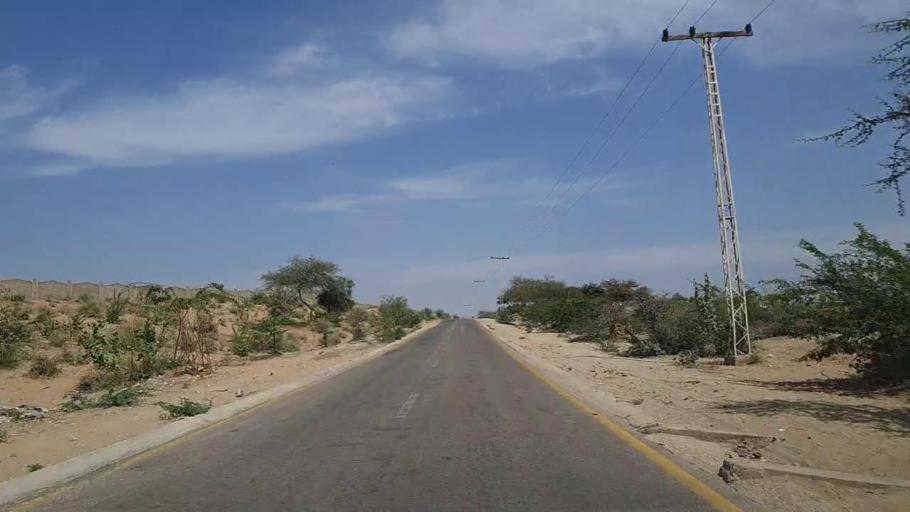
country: PK
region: Sindh
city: Mithi
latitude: 24.7663
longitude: 69.7978
